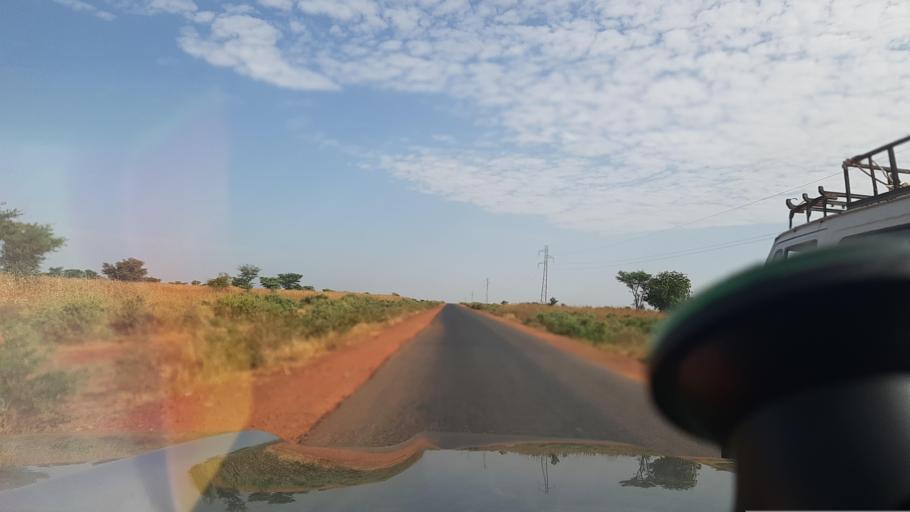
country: ML
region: Segou
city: Segou
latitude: 13.5408
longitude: -6.1216
